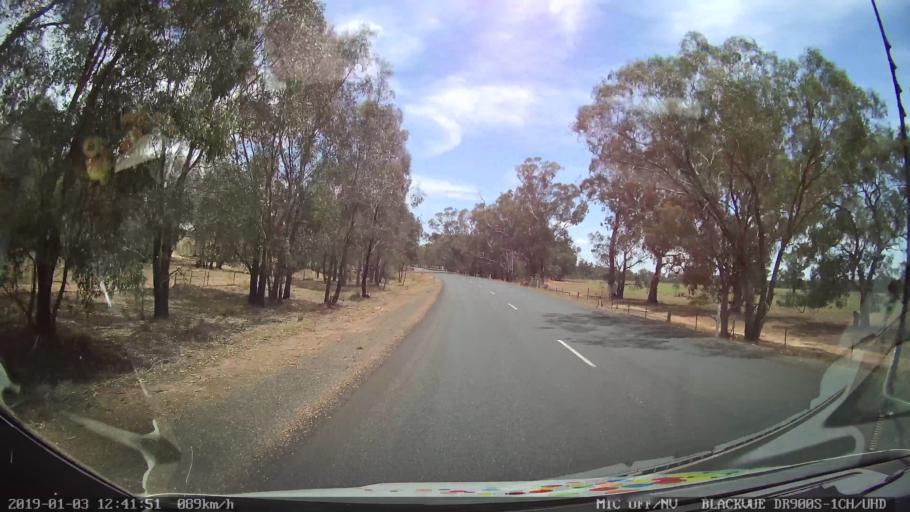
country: AU
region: New South Wales
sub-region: Weddin
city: Grenfell
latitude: -33.7942
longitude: 148.2153
